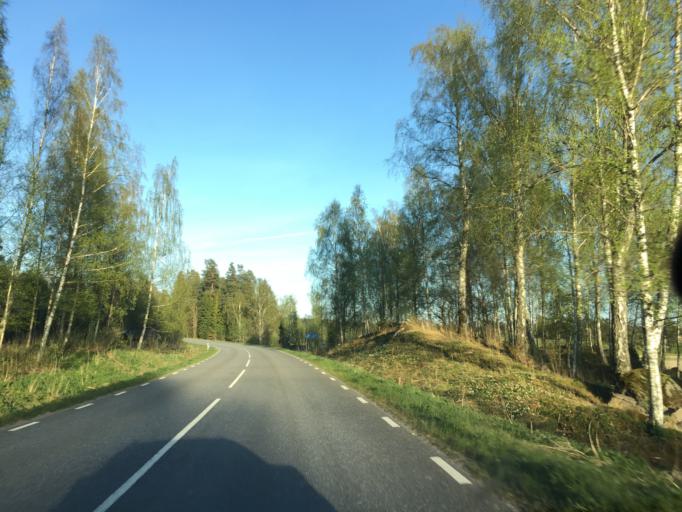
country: SE
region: OErebro
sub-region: Orebro Kommun
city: Hovsta
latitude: 59.3846
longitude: 15.1915
